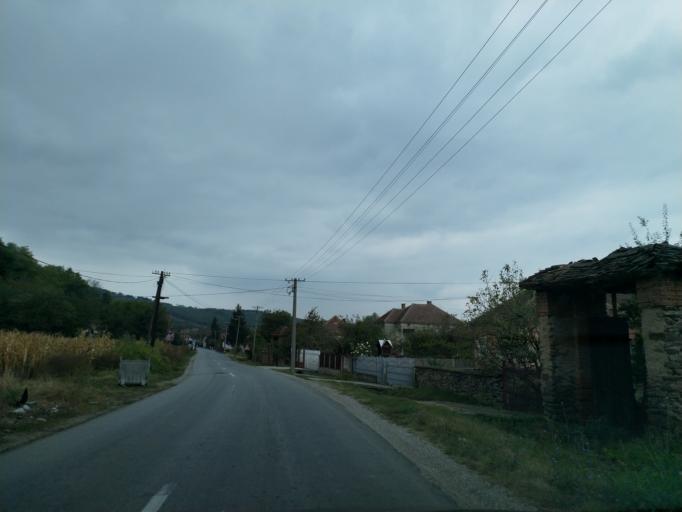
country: RS
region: Central Serbia
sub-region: Pomoravski Okrug
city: Jagodina
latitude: 44.0647
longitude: 21.1813
